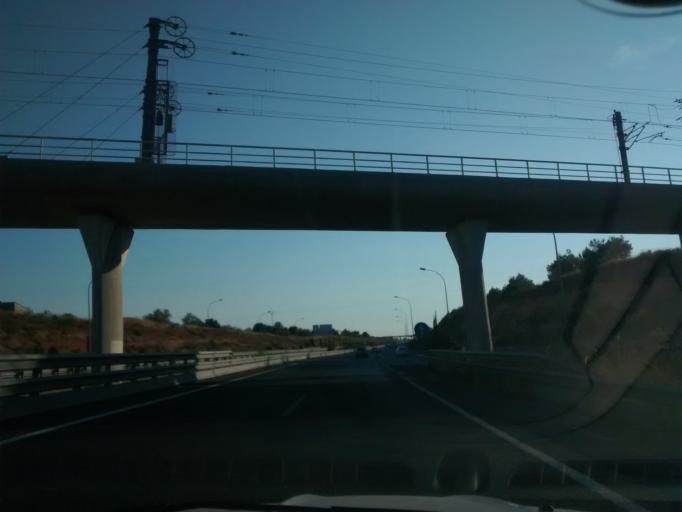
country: ES
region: Balearic Islands
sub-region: Illes Balears
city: Inca
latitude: 39.7130
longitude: 2.9200
